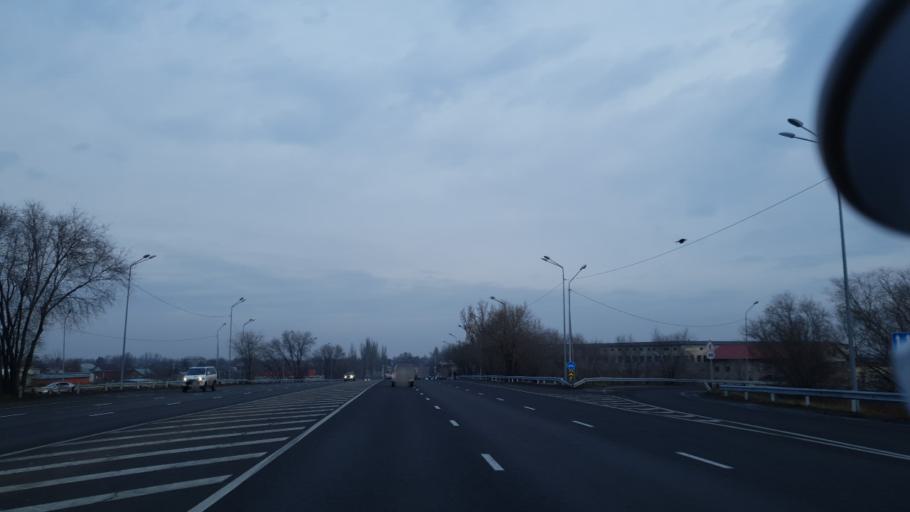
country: KZ
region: Almaty Oblysy
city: Pervomayskiy
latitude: 43.3548
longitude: 76.9389
